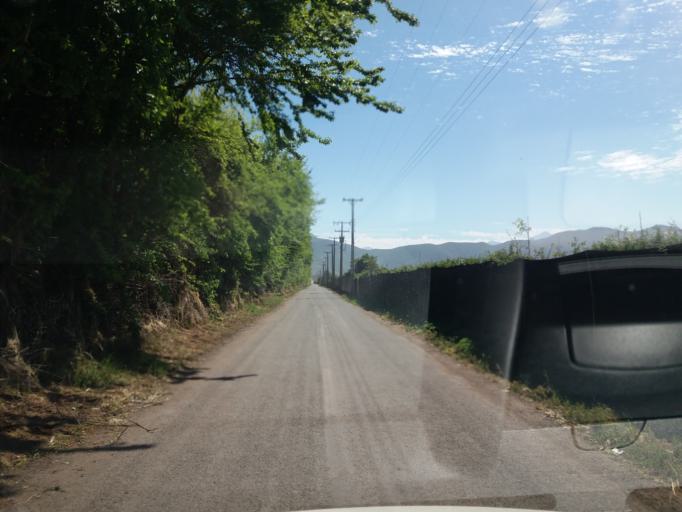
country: CL
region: Valparaiso
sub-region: Provincia de Quillota
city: Quillota
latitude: -32.8673
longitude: -71.2135
